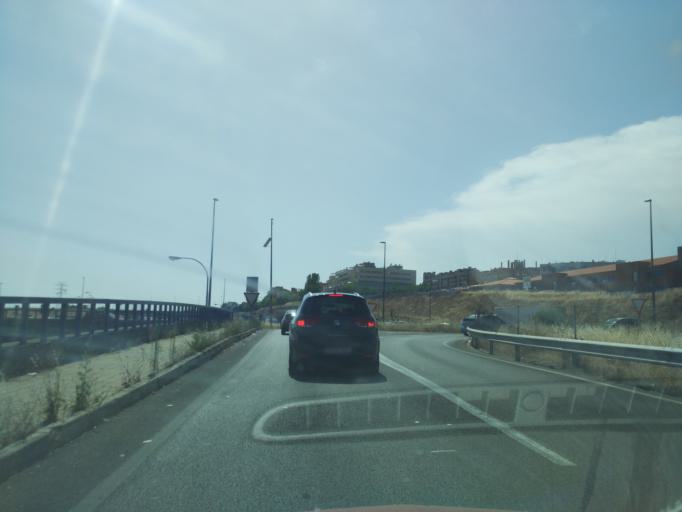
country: ES
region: Madrid
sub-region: Provincia de Madrid
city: Latina
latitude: 40.3622
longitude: -3.7436
